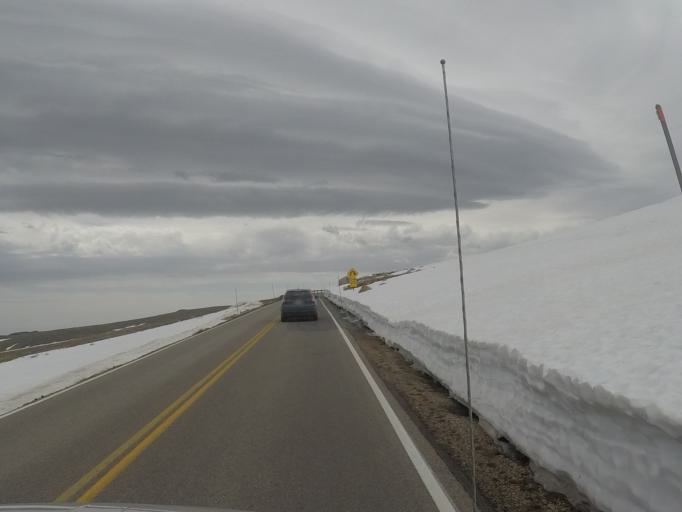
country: US
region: Montana
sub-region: Carbon County
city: Red Lodge
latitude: 44.9766
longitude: -109.4282
